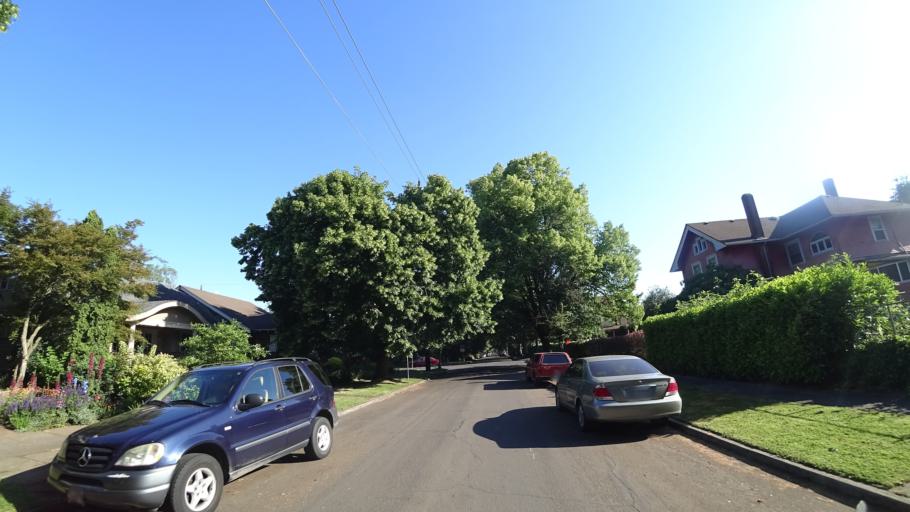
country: US
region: Oregon
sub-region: Multnomah County
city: Portland
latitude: 45.5660
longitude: -122.6669
